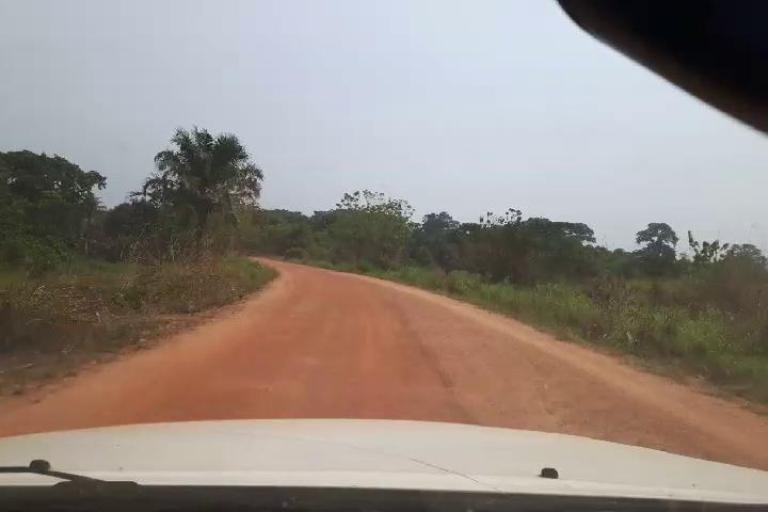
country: SL
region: Northern Province
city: Masingbi
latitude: 8.8803
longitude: -11.8200
